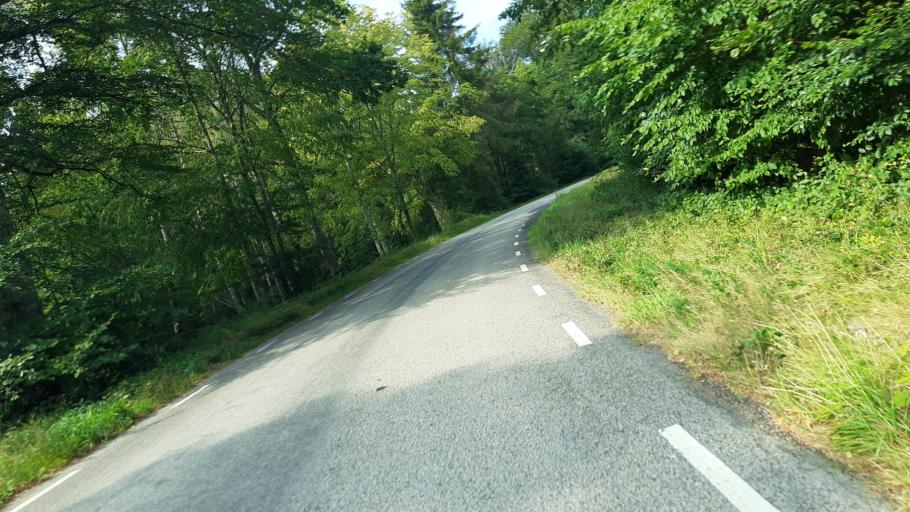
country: SE
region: Blekinge
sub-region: Karlskrona Kommun
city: Nattraby
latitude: 56.2174
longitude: 15.4400
